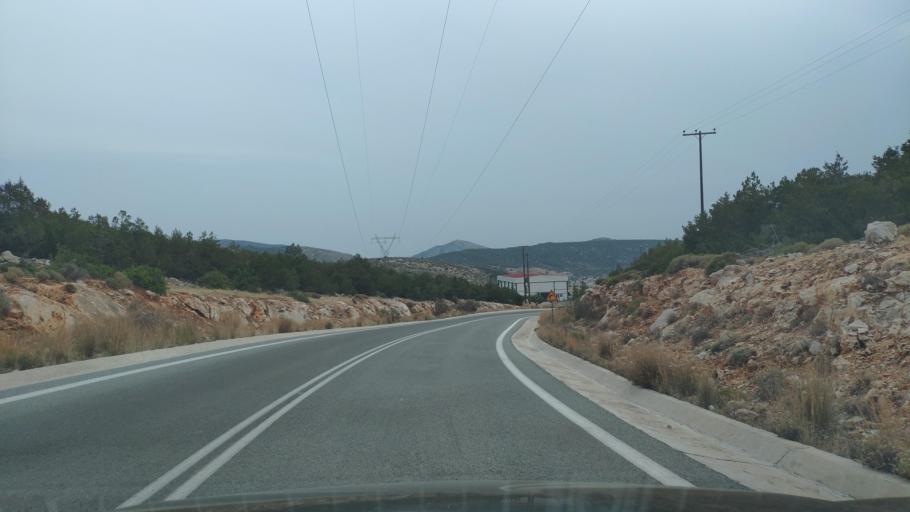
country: GR
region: Peloponnese
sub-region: Nomos Argolidos
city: Didyma
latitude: 37.4468
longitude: 23.1887
